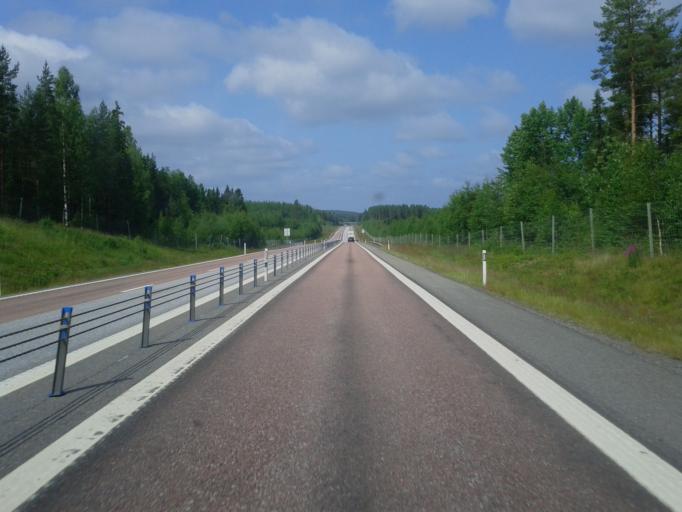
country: SE
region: Vaesterbotten
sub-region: Skelleftea Kommun
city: Soedra Bergsbyn
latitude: 64.6912
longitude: 21.0369
